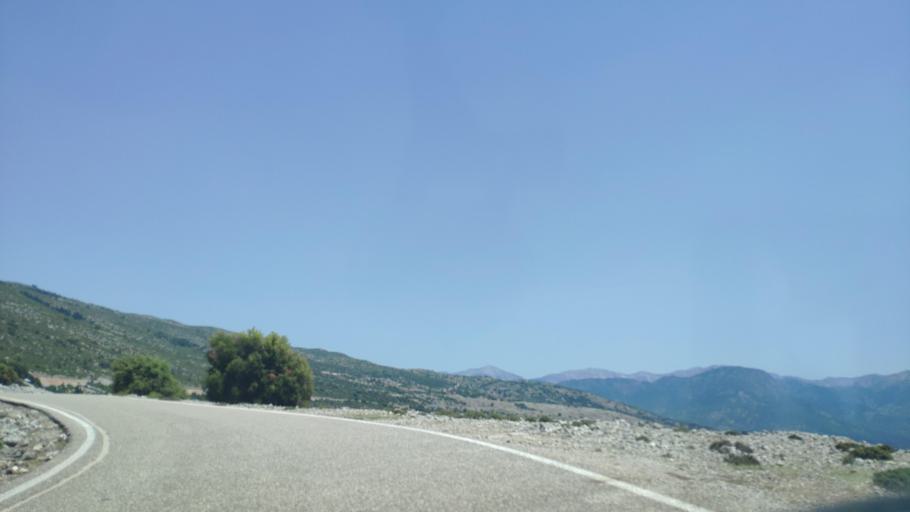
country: GR
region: West Greece
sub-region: Nomos Aitolias kai Akarnanias
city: Krikellos
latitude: 39.0592
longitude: 21.3839
